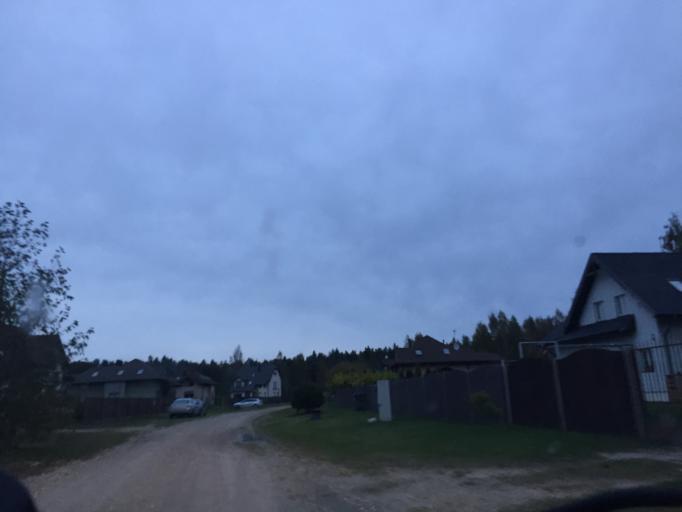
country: LV
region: Adazi
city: Adazi
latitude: 57.0881
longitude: 24.3753
